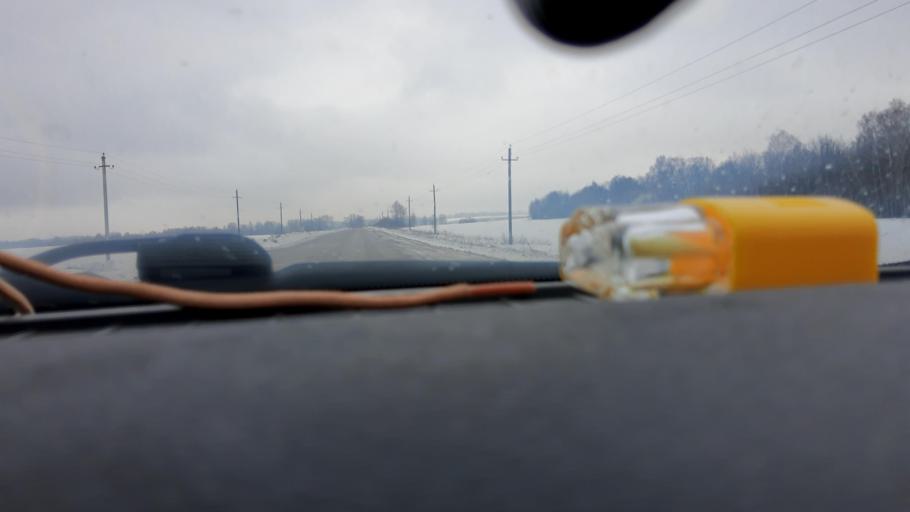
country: RU
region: Bashkortostan
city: Iglino
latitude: 54.6958
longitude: 56.4166
